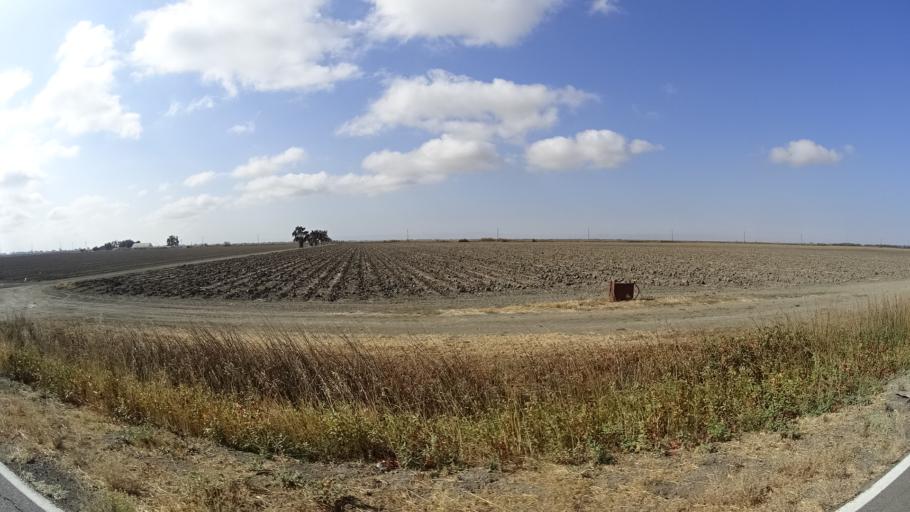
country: US
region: California
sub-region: Yolo County
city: Woodland
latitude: 38.8305
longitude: -121.7497
